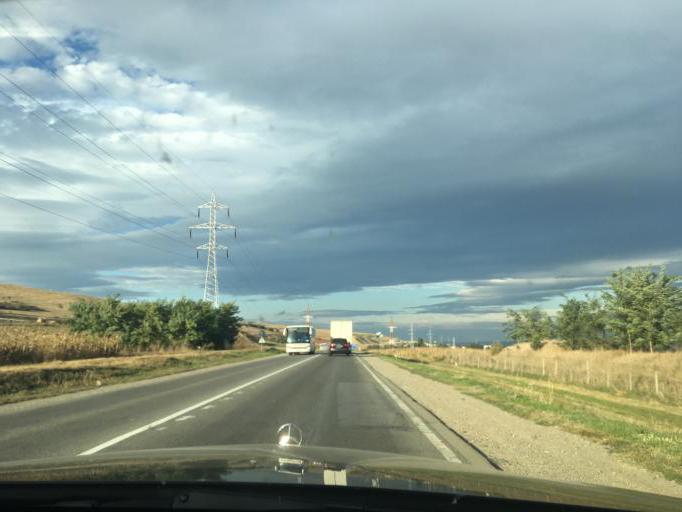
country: RO
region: Alba
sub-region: Comuna Santimbru
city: Santimbru
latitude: 46.1298
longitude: 23.6280
